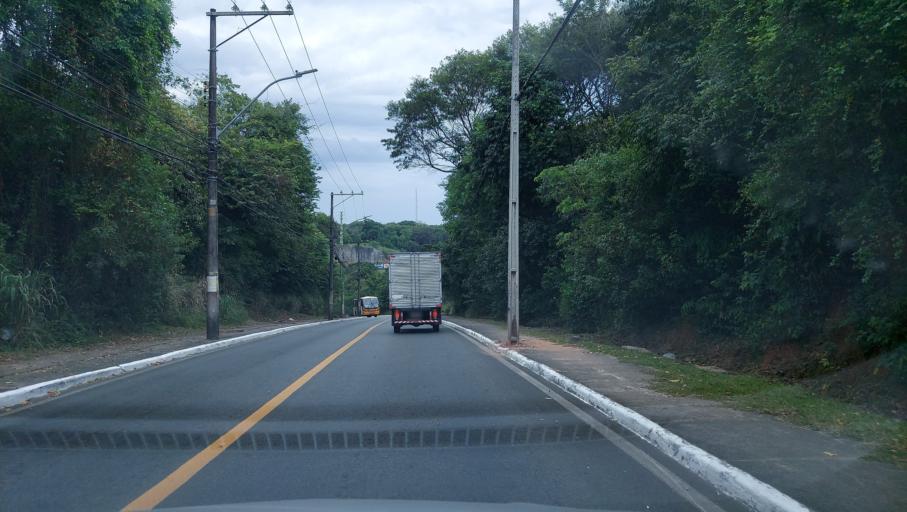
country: BR
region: Bahia
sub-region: Salvador
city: Salvador
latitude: -12.9673
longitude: -38.4434
